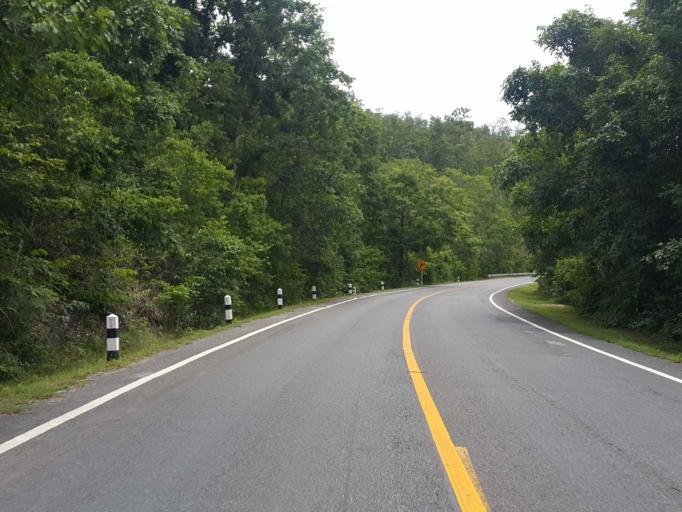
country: TH
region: Chiang Mai
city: Chom Thong
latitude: 18.5158
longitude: 98.6581
